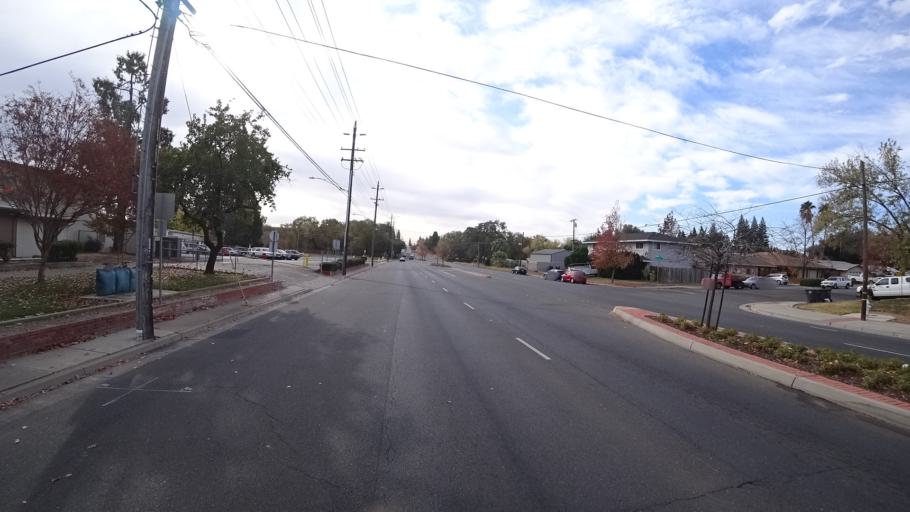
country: US
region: California
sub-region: Sacramento County
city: Citrus Heights
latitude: 38.6999
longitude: -121.2717
